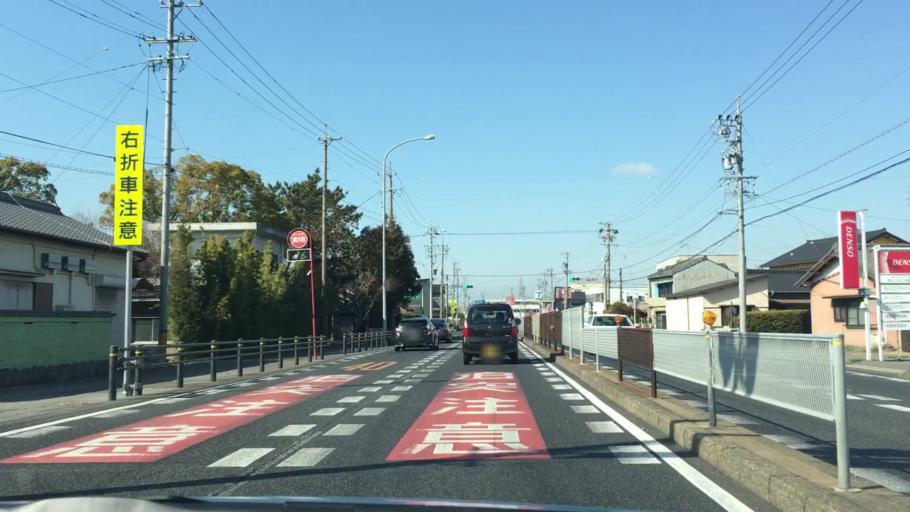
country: JP
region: Aichi
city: Okazaki
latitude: 34.9665
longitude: 137.1335
